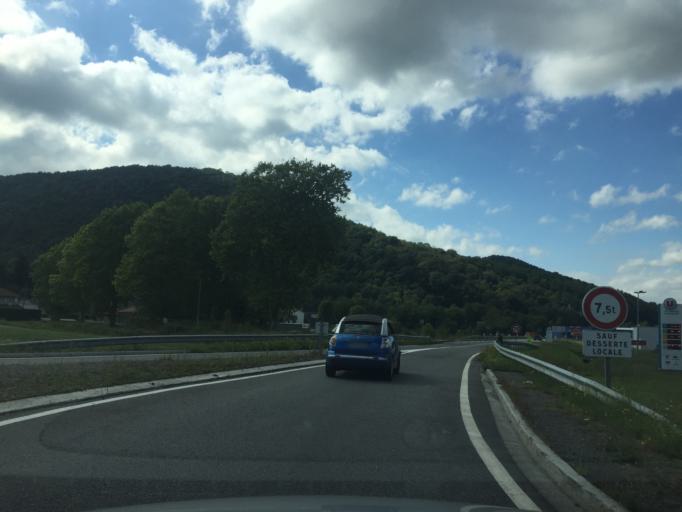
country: FR
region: Midi-Pyrenees
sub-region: Departement de la Haute-Garonne
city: Gourdan-Polignan
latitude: 43.0599
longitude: 0.5926
